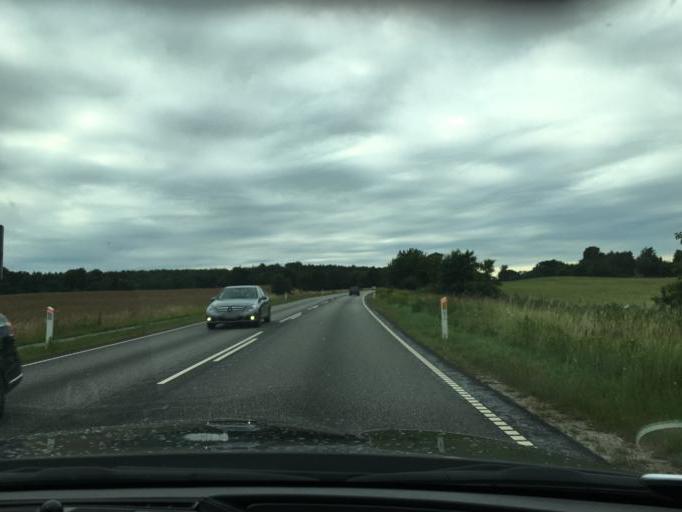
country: DK
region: Capital Region
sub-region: Horsholm Kommune
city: Horsholm
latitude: 55.8776
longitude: 12.4731
